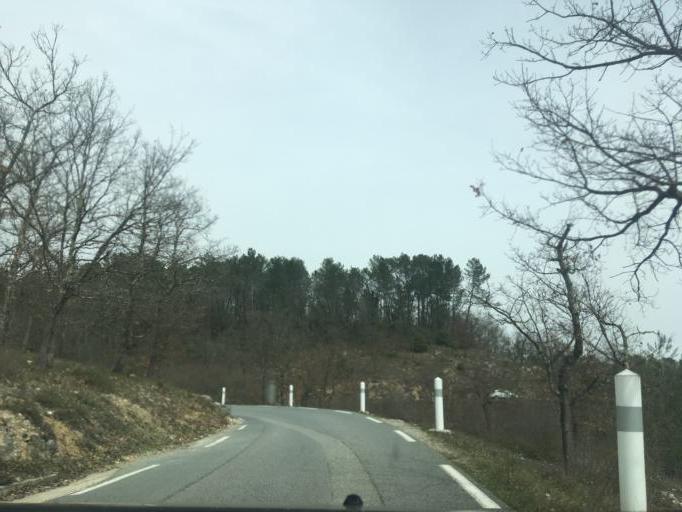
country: FR
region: Provence-Alpes-Cote d'Azur
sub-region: Departement du Var
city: Saint-Paul-en-Foret
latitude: 43.5865
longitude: 6.7298
